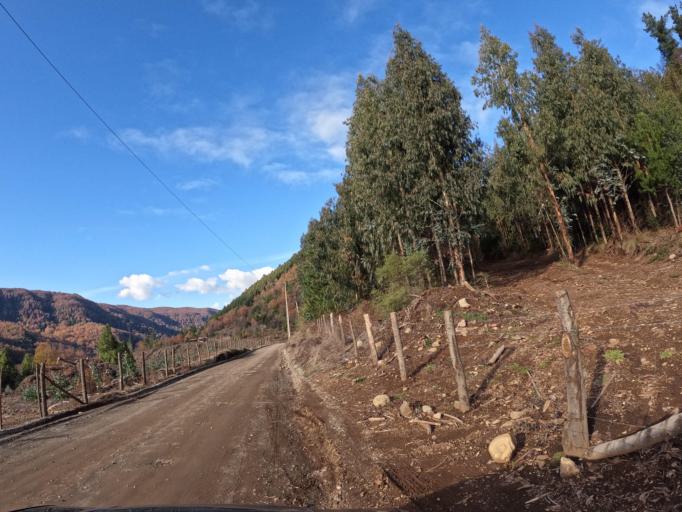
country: CL
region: Biobio
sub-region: Provincia de Nuble
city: Coihueco
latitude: -36.8005
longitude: -71.6907
